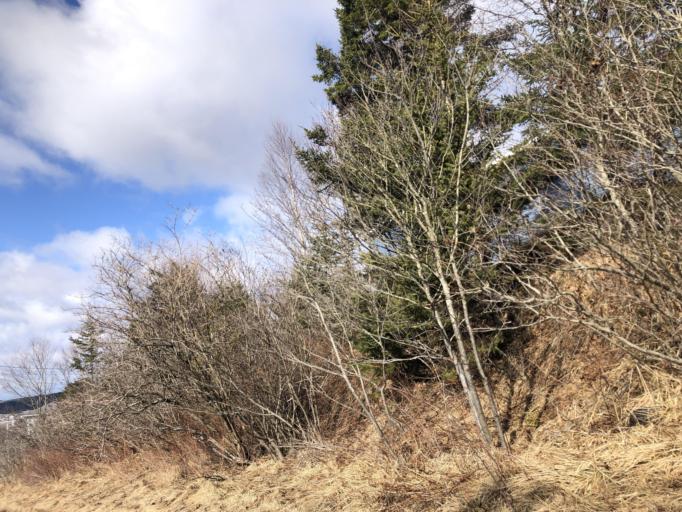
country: CA
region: New Brunswick
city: Saint John
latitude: 45.3196
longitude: -66.0052
